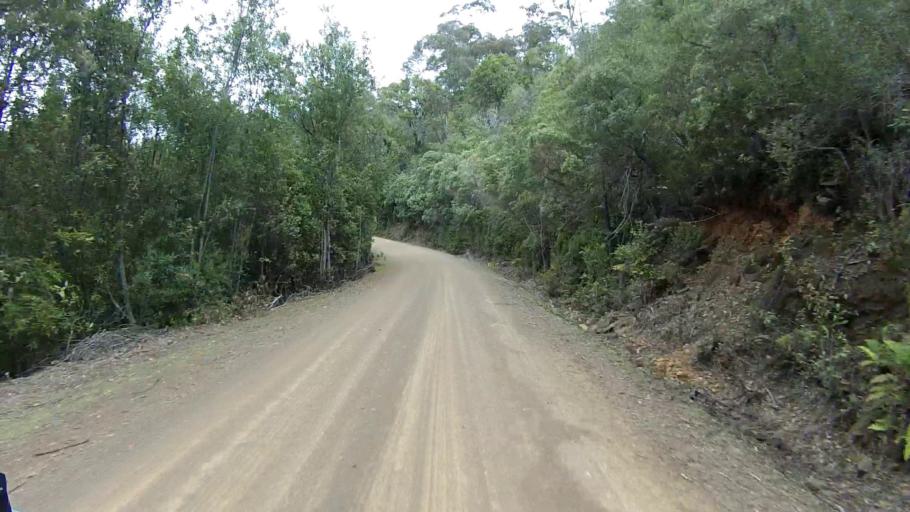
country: AU
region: Tasmania
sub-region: Sorell
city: Sorell
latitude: -42.6050
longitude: 147.8806
